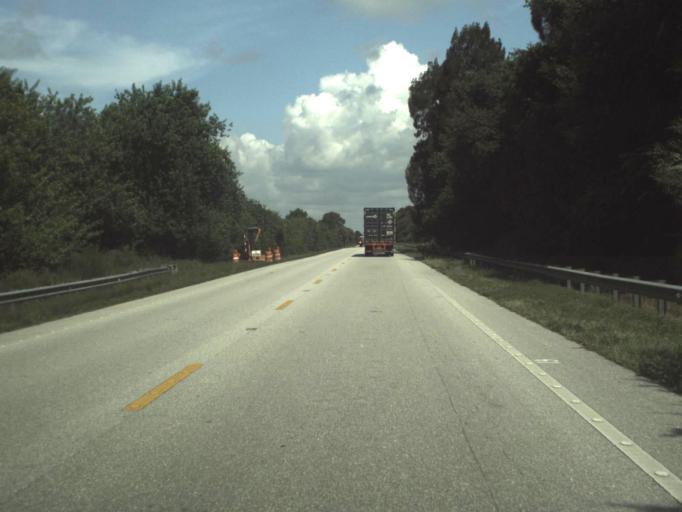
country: US
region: Florida
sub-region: Okeechobee County
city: Taylor Creek
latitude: 27.1480
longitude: -80.6607
